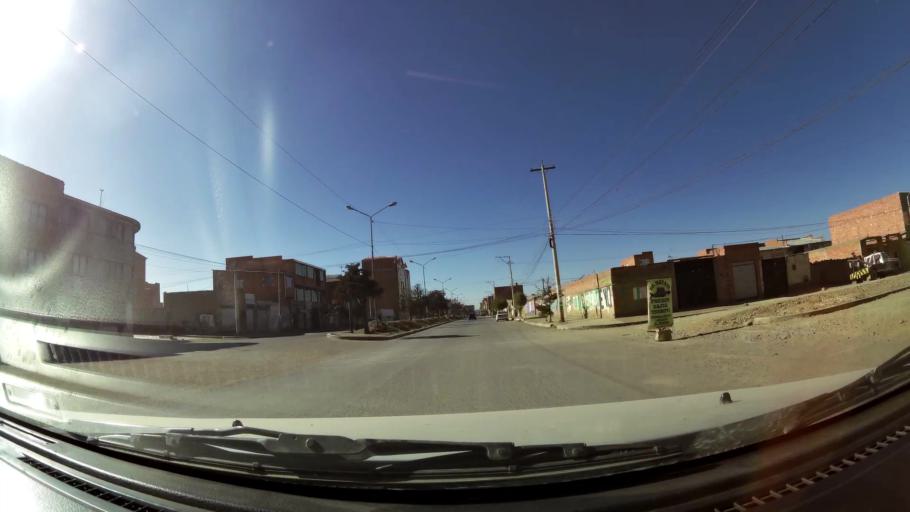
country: BO
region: La Paz
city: La Paz
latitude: -16.5162
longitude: -68.2110
